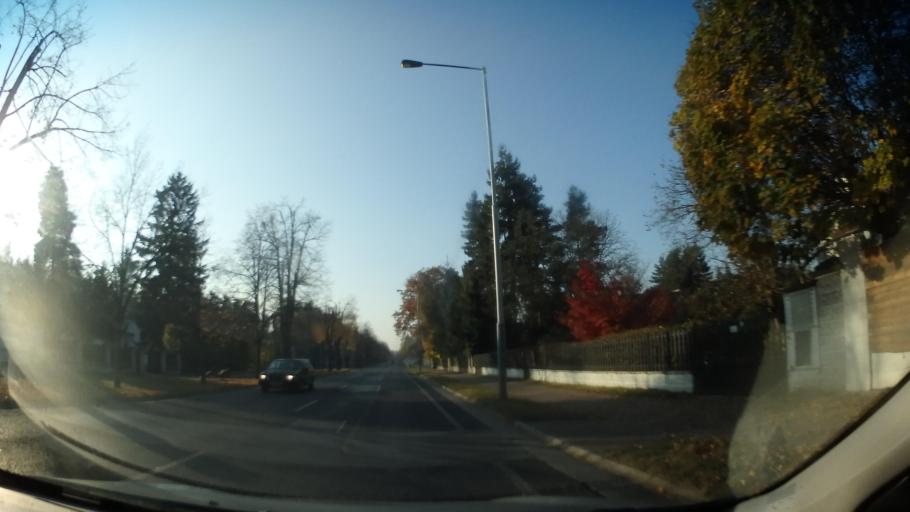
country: CZ
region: Central Bohemia
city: Sestajovice
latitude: 50.0942
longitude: 14.6685
